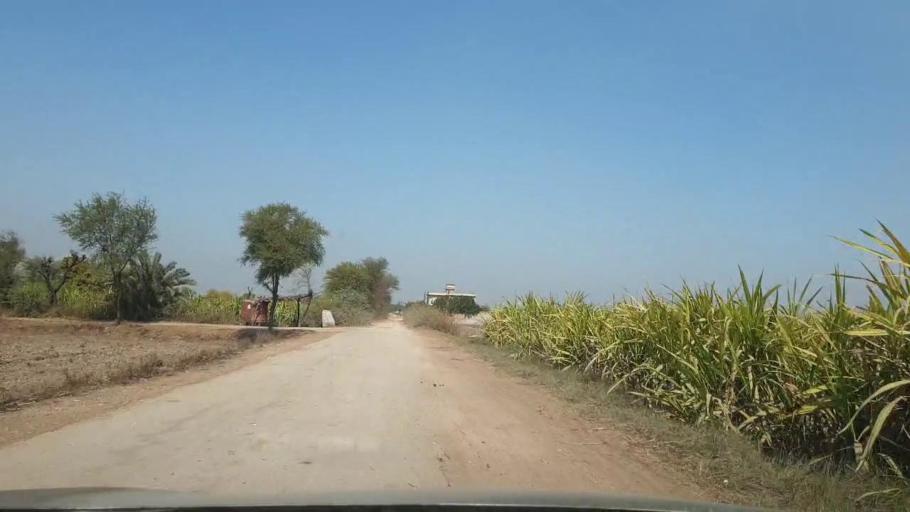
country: PK
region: Sindh
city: Tando Adam
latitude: 25.6150
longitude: 68.6462
